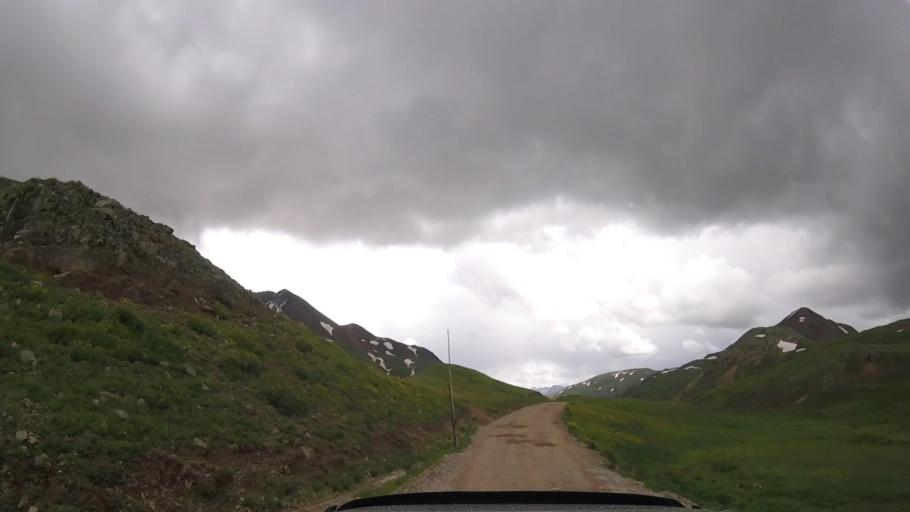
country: US
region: Colorado
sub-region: Ouray County
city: Ouray
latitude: 37.9567
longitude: -107.5752
